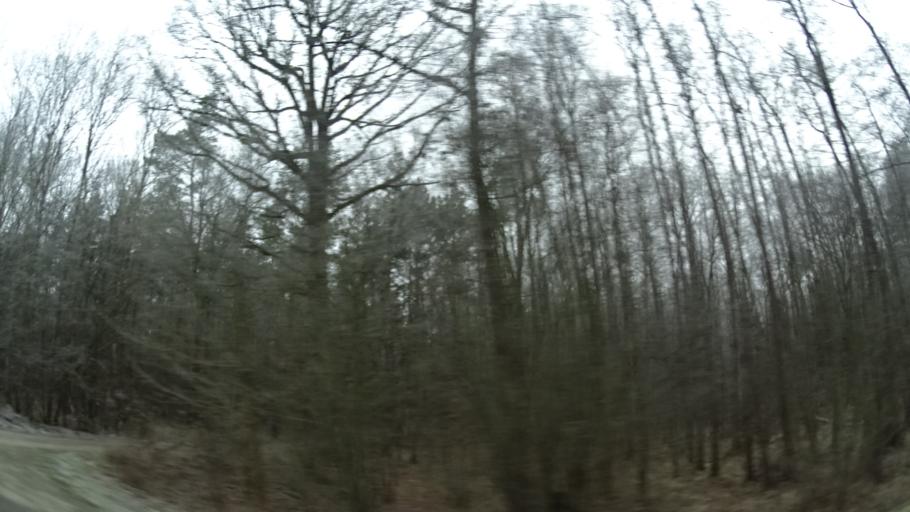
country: DE
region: Bavaria
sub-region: Regierungsbezirk Unterfranken
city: Albertshofen
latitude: 49.7704
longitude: 10.1976
